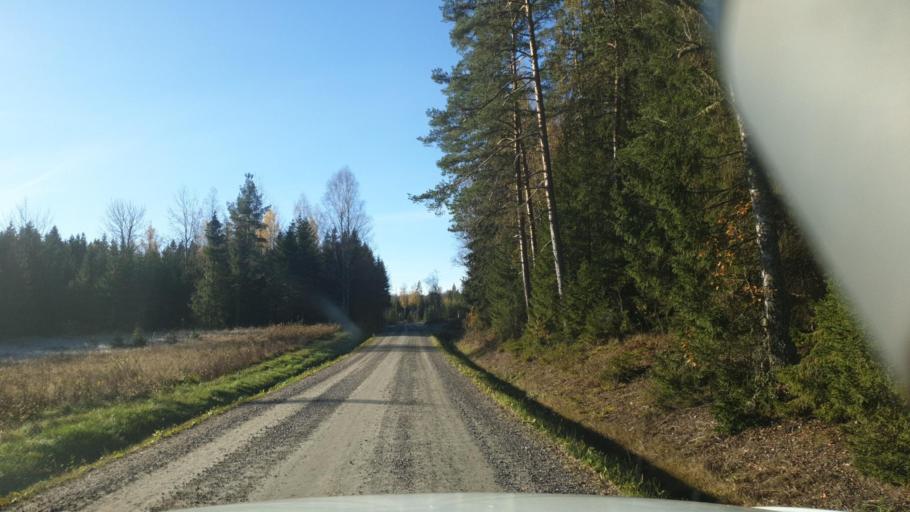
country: SE
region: Vaermland
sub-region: Karlstads Kommun
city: Edsvalla
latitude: 59.5462
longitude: 13.0075
